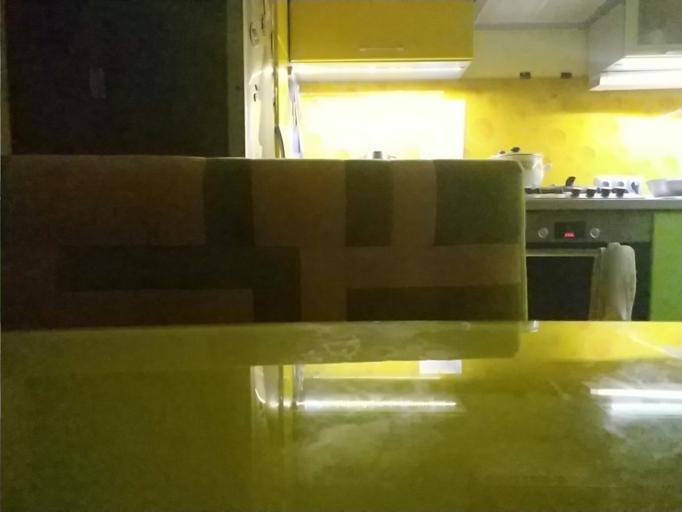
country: RU
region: Republic of Karelia
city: Pyaozerskiy
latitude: 65.9106
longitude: 30.4225
